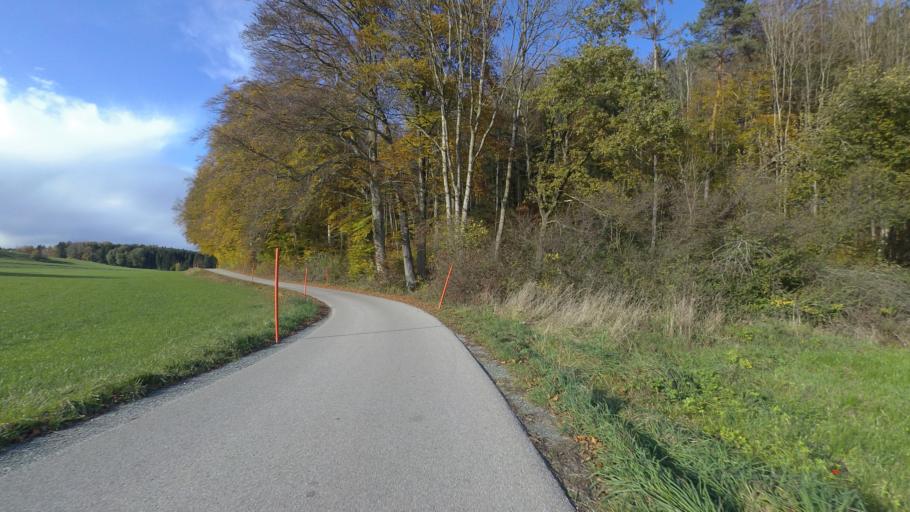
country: DE
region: Bavaria
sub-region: Upper Bavaria
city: Nussdorf
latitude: 47.9200
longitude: 12.5755
